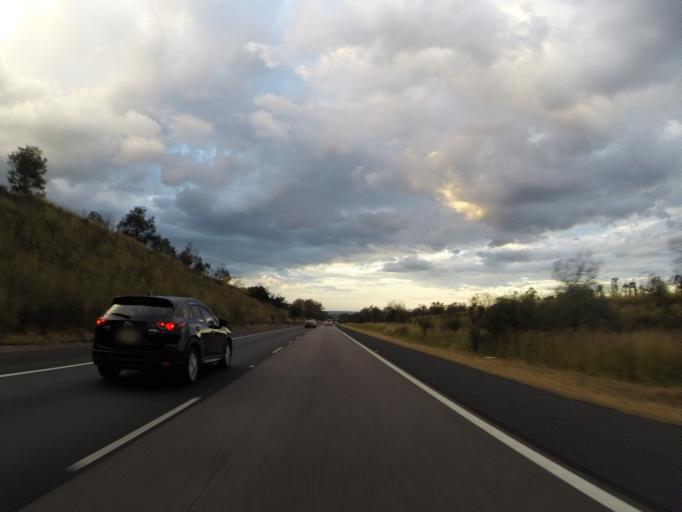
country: AU
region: New South Wales
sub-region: Wollondilly
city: Douglas Park
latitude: -34.2193
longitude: 150.6782
